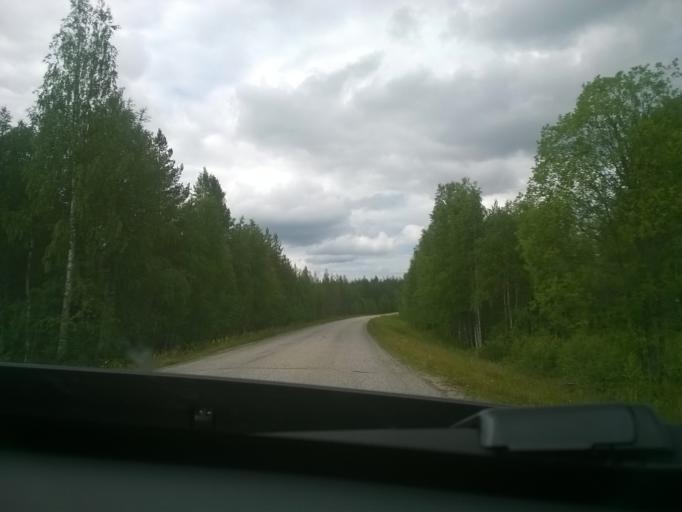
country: FI
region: Kainuu
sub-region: Kehys-Kainuu
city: Kuhmo
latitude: 64.3874
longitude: 29.7916
